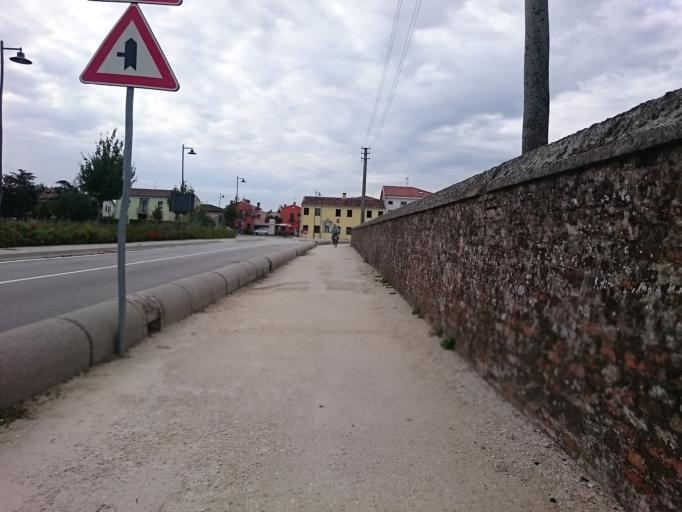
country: IT
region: Veneto
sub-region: Provincia di Vicenza
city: Grumolo delle Abbadesse
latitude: 45.4980
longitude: 11.6686
